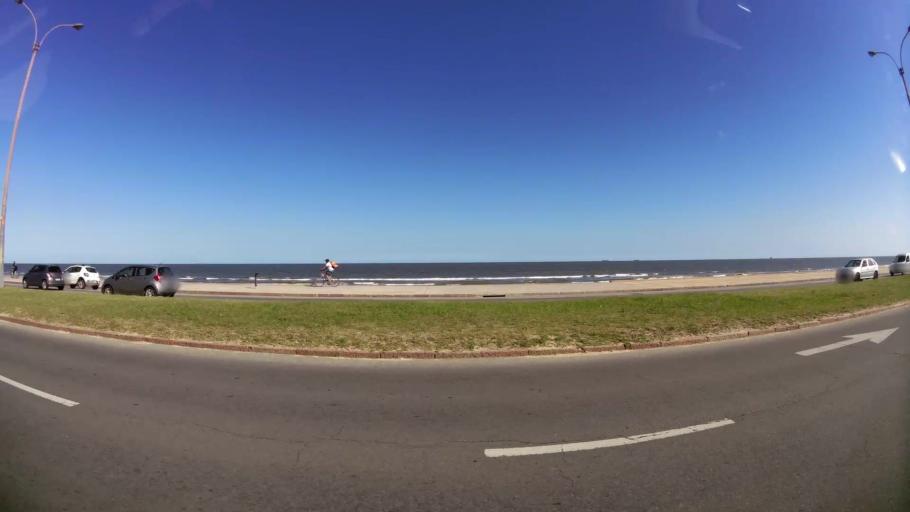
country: UY
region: Canelones
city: Barra de Carrasco
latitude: -34.8902
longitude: -56.0526
